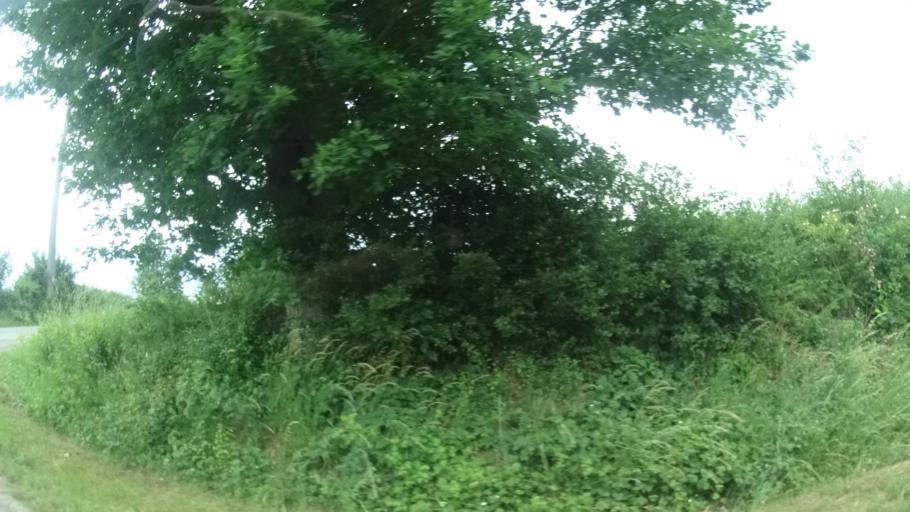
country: DE
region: Hesse
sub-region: Regierungsbezirk Giessen
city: Schlitz
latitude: 50.6747
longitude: 9.5408
